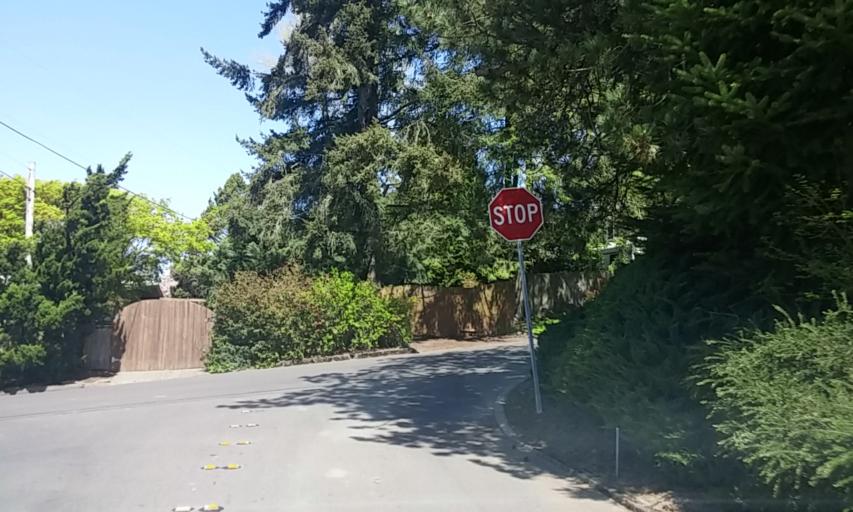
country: US
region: Oregon
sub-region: Washington County
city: West Haven
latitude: 45.5194
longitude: -122.7671
